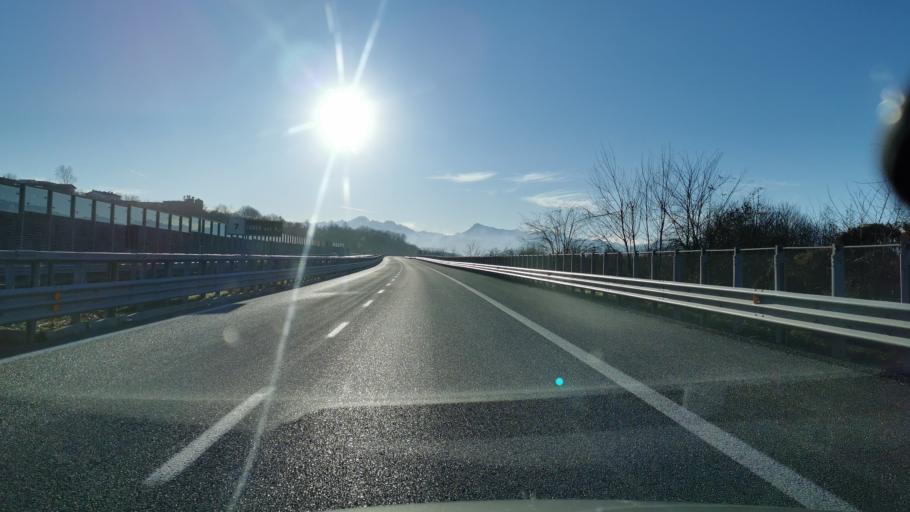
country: IT
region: Piedmont
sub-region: Provincia di Cuneo
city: Castelletto Stura
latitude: 44.4471
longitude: 7.6368
